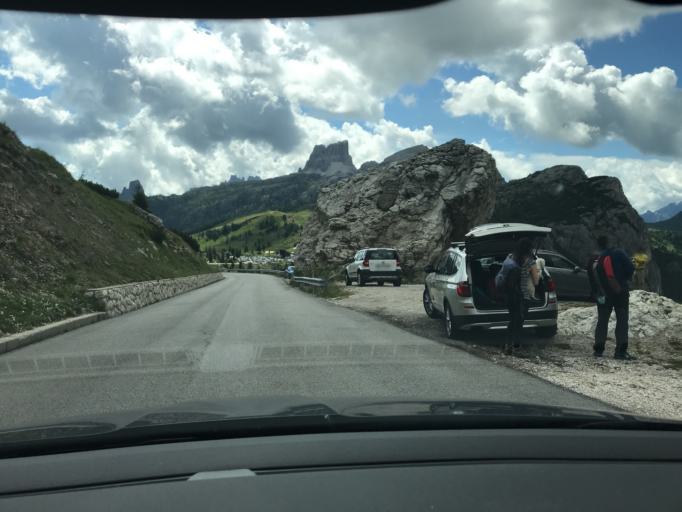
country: IT
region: Veneto
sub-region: Provincia di Belluno
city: Livinallongo del Col di Lana
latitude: 46.5231
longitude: 12.0004
